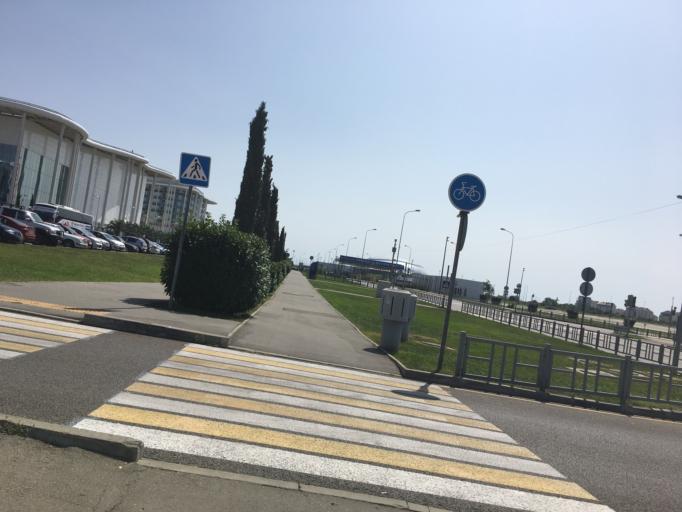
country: RU
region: Krasnodarskiy
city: Adler
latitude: 43.4144
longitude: 39.9482
